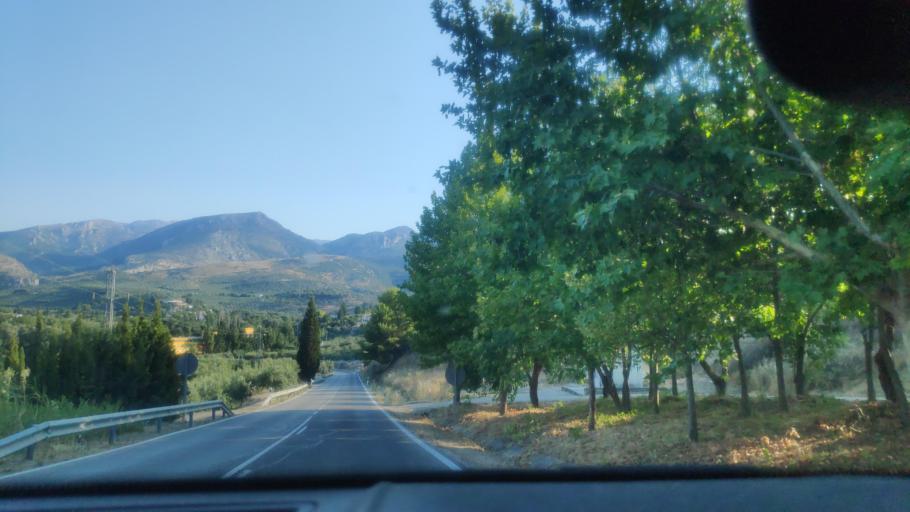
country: ES
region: Andalusia
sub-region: Provincia de Jaen
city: Jaen
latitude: 37.7269
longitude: -3.7628
